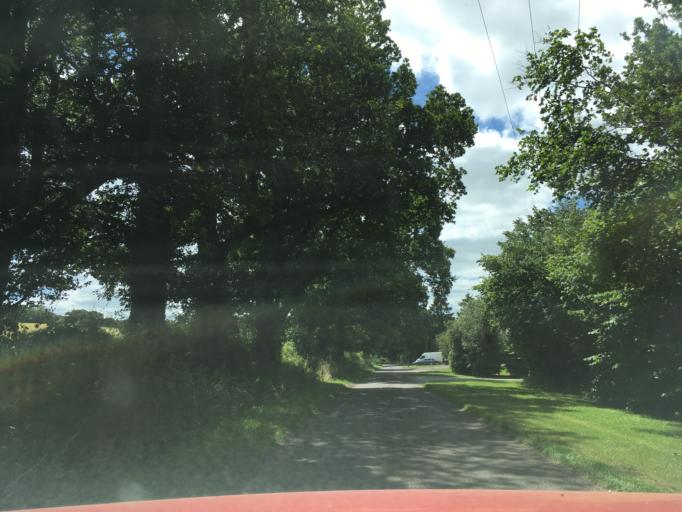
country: GB
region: England
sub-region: Hampshire
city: Highclere
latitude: 51.2850
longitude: -1.4167
